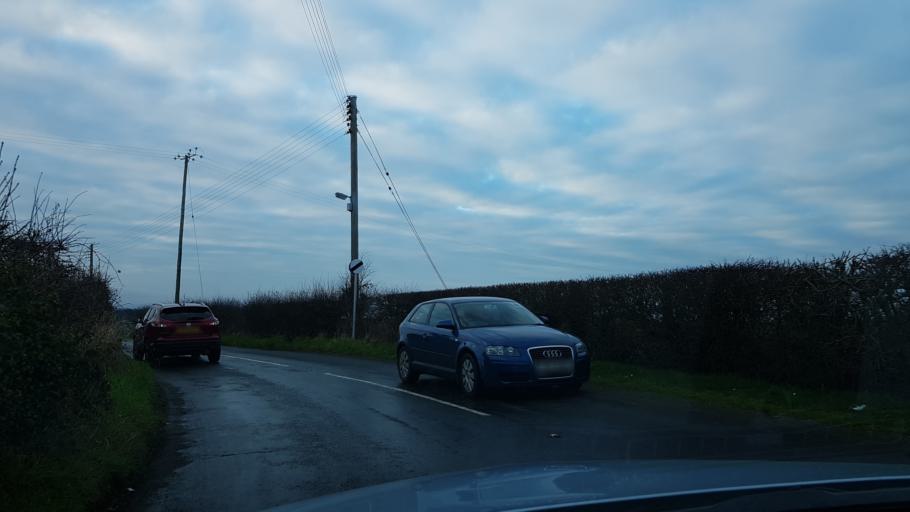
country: GB
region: Northern Ireland
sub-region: Down District
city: Donaghadee
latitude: 54.6724
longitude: -5.5841
